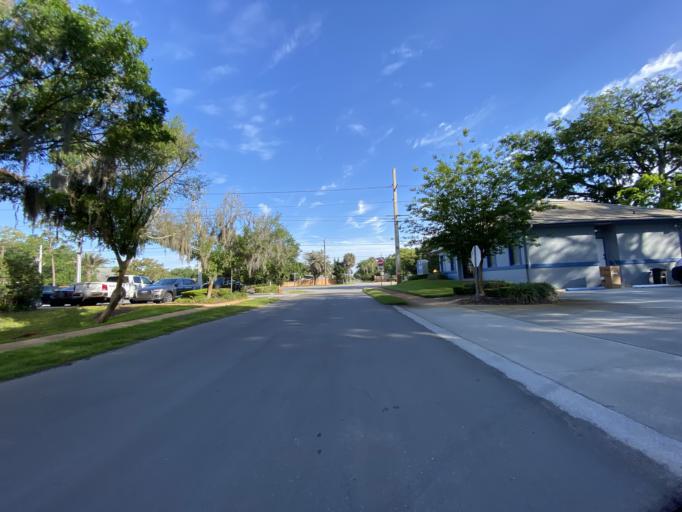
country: US
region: Florida
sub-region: Volusia County
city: South Daytona
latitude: 29.1778
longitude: -81.0214
